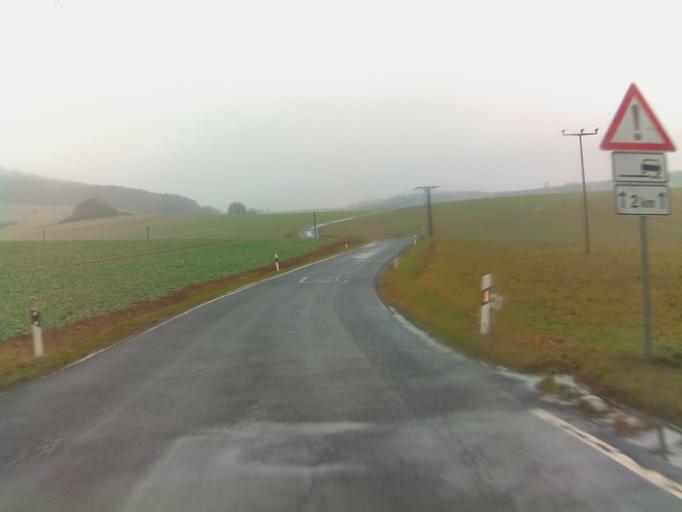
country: DE
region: Thuringia
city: Dingsleben
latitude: 50.4222
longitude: 10.6168
